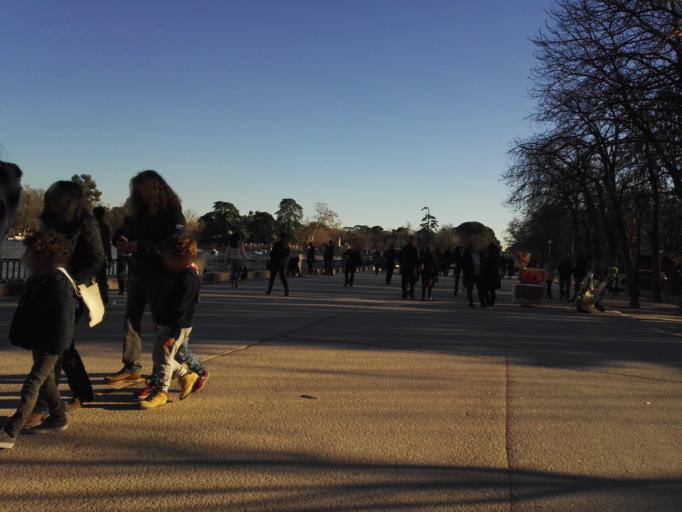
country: ES
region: Madrid
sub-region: Provincia de Madrid
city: Retiro
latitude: 40.4175
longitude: -3.6850
